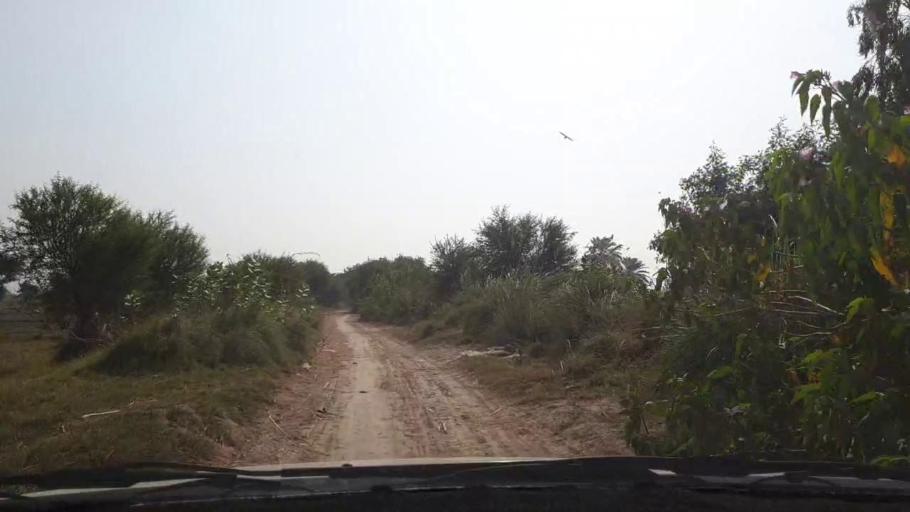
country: PK
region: Sindh
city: Tando Muhammad Khan
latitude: 25.0812
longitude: 68.3607
